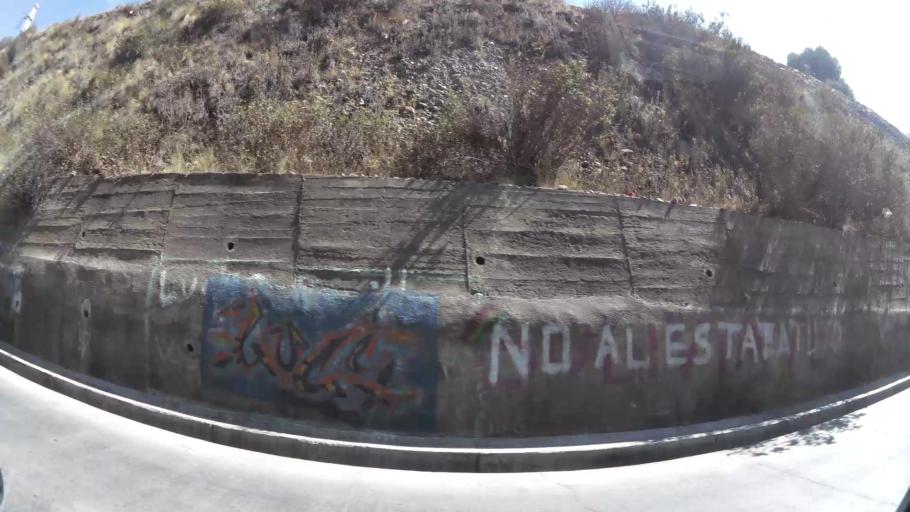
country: BO
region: La Paz
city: La Paz
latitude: -16.5330
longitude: -68.1485
